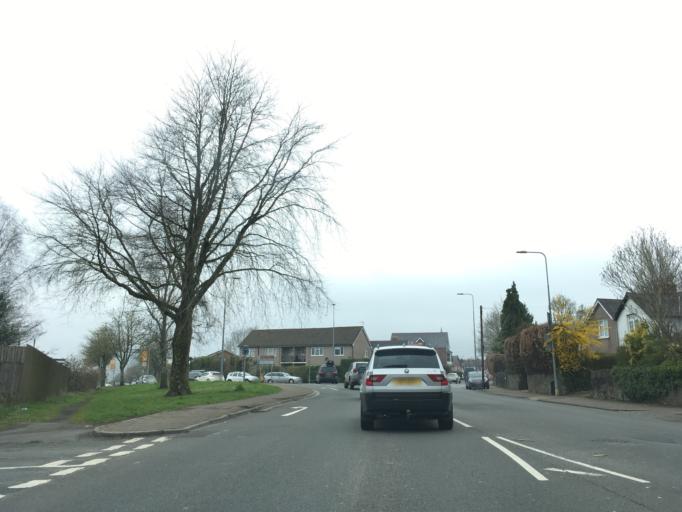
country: GB
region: Wales
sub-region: Cardiff
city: Cardiff
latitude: 51.5275
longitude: -3.1818
